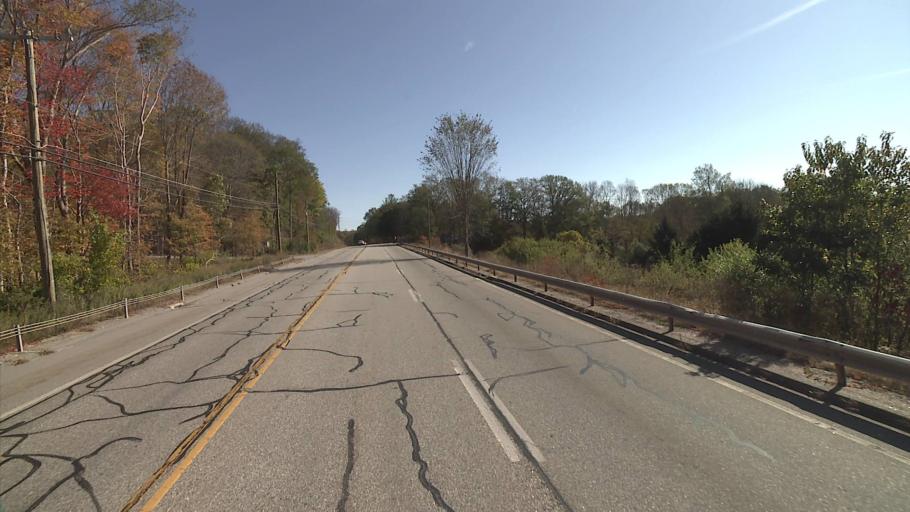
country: US
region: Connecticut
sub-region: Windham County
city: Windham
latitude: 41.7673
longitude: -72.1109
